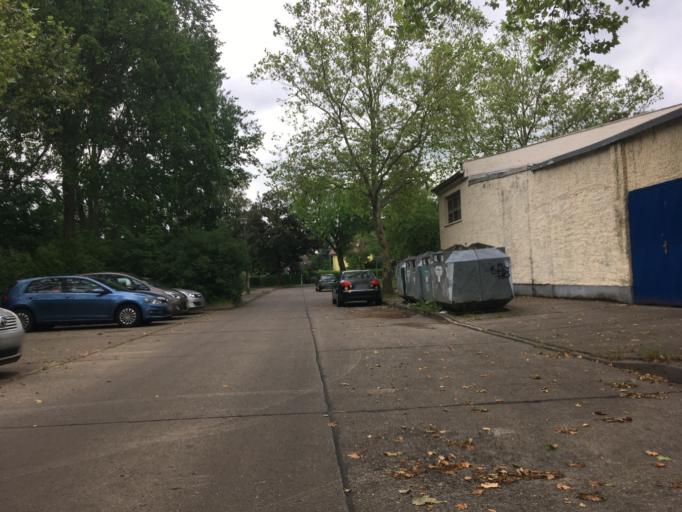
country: DE
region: Berlin
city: Friedrichshagen
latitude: 52.4513
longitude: 13.6391
